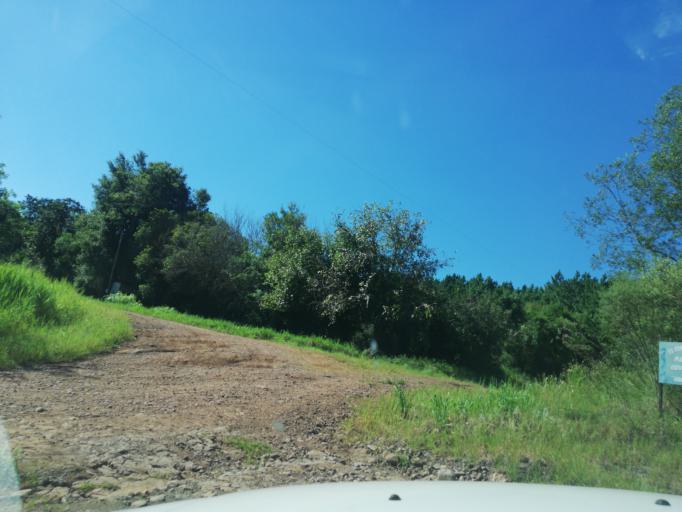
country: AR
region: Misiones
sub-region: Departamento de Leandro N. Alem
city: Leandro N. Alem
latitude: -27.5756
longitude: -55.3708
